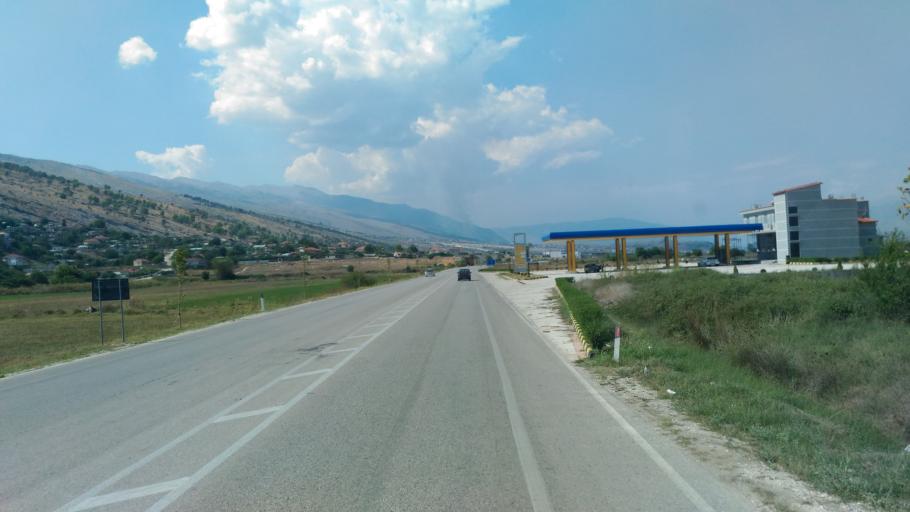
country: AL
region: Gjirokaster
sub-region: Rrethi i Gjirokastres
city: Dervician
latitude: 40.0142
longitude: 20.1992
